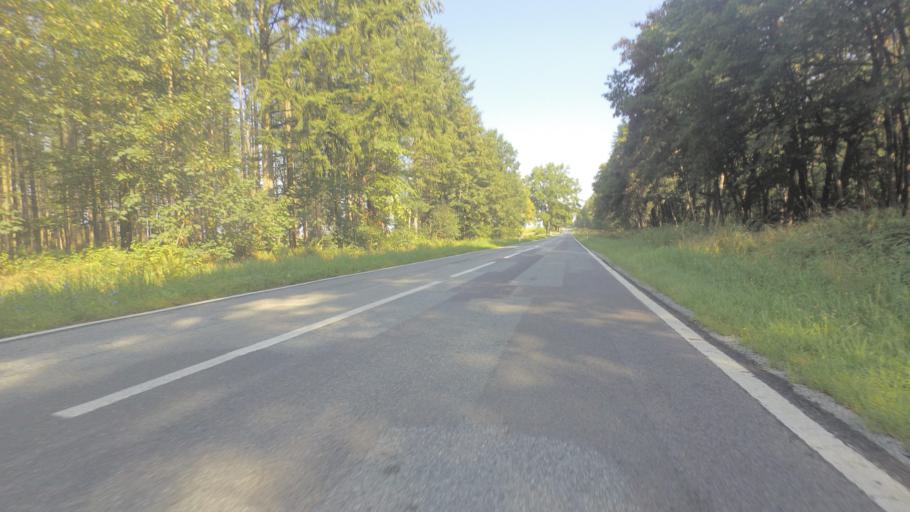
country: DE
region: Mecklenburg-Vorpommern
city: Grabowhofe
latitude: 53.5967
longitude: 12.4711
